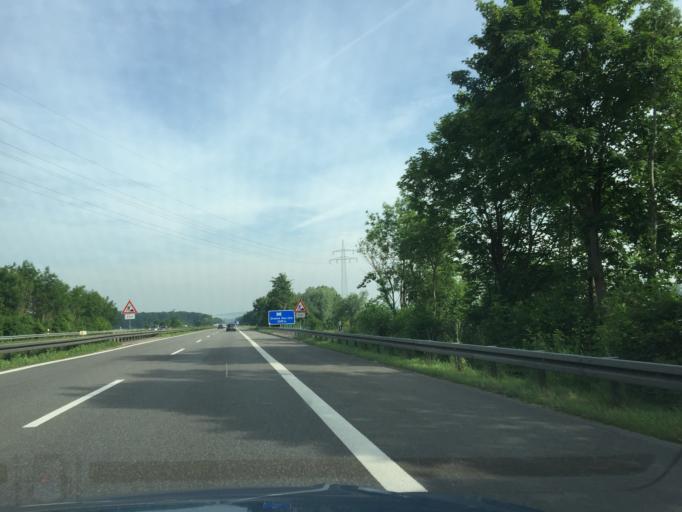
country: DE
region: Bavaria
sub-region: Swabia
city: Neu-Ulm
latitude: 48.3534
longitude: 10.0129
